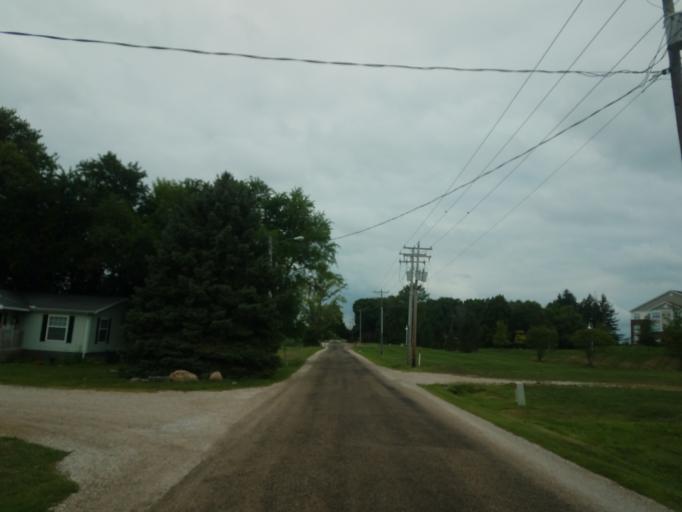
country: US
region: Illinois
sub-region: McLean County
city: Bloomington
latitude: 40.4444
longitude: -89.0098
